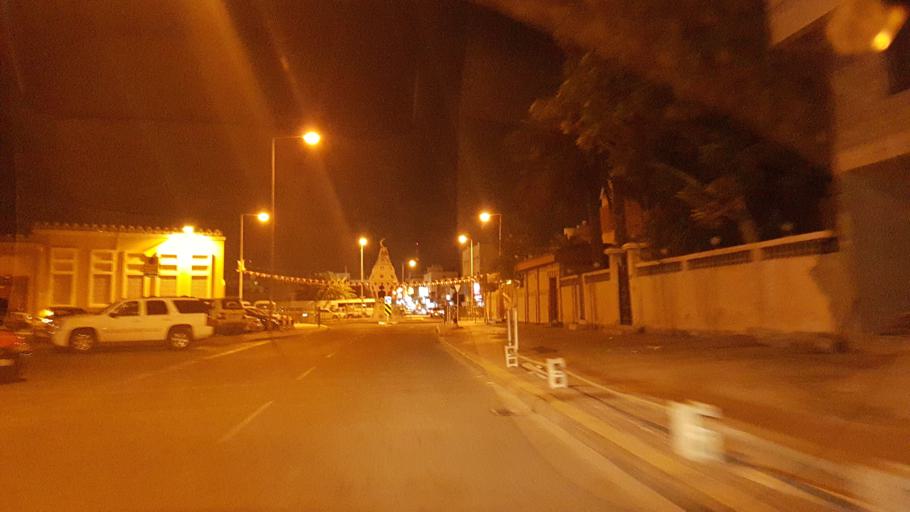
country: BH
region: Muharraq
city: Al Hadd
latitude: 26.2425
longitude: 50.6556
